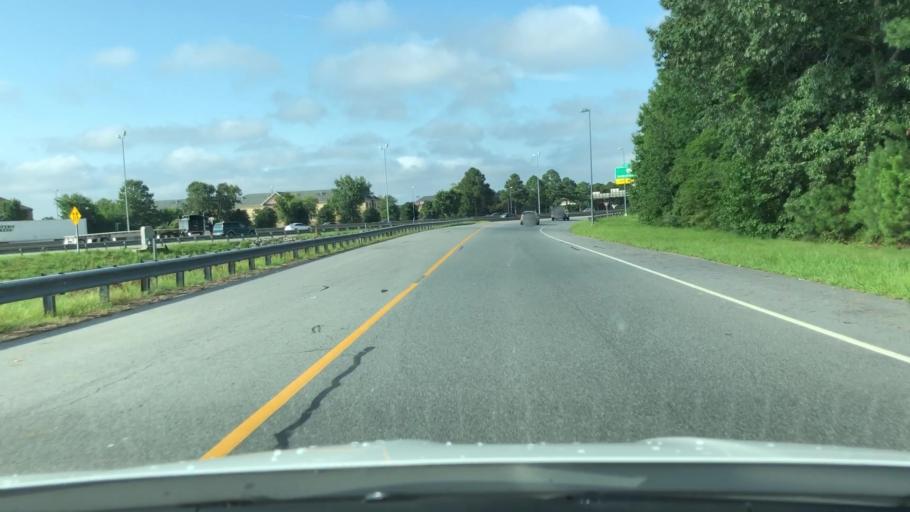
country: US
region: Virginia
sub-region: City of Chesapeake
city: Chesapeake
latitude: 36.7839
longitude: -76.2371
